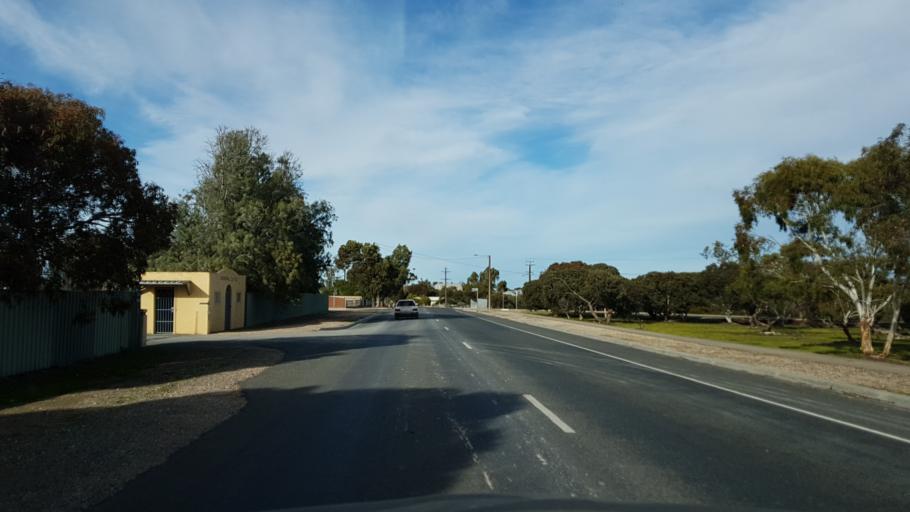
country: AU
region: South Australia
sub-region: Murray Bridge
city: Tailem Bend
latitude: -35.2488
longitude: 139.4551
